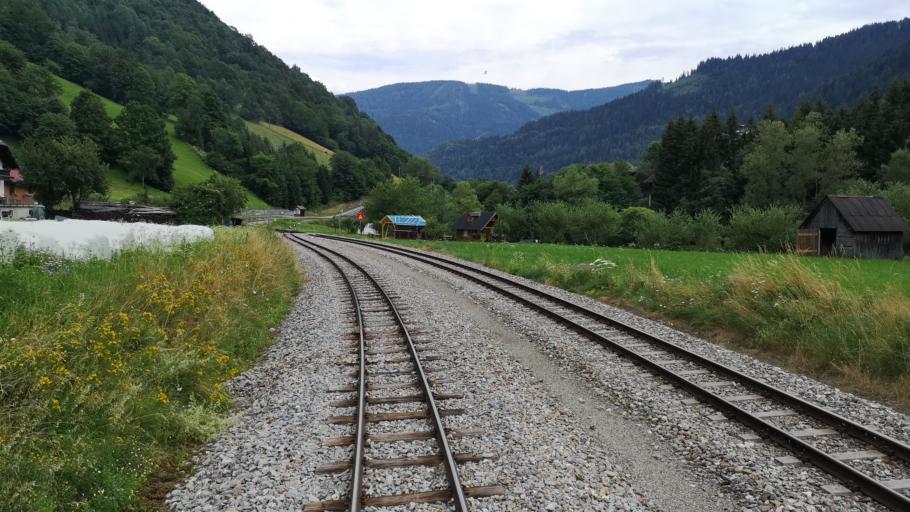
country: AT
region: Salzburg
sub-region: Politischer Bezirk Tamsweg
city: Ramingstein
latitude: 47.0695
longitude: 13.8798
